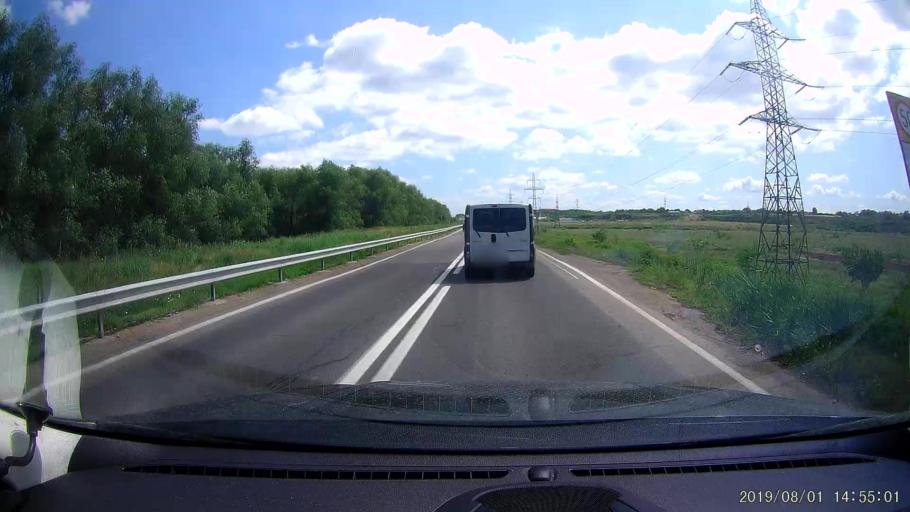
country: RO
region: Braila
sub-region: Municipiul Braila
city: Braila
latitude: 45.3101
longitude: 27.9829
